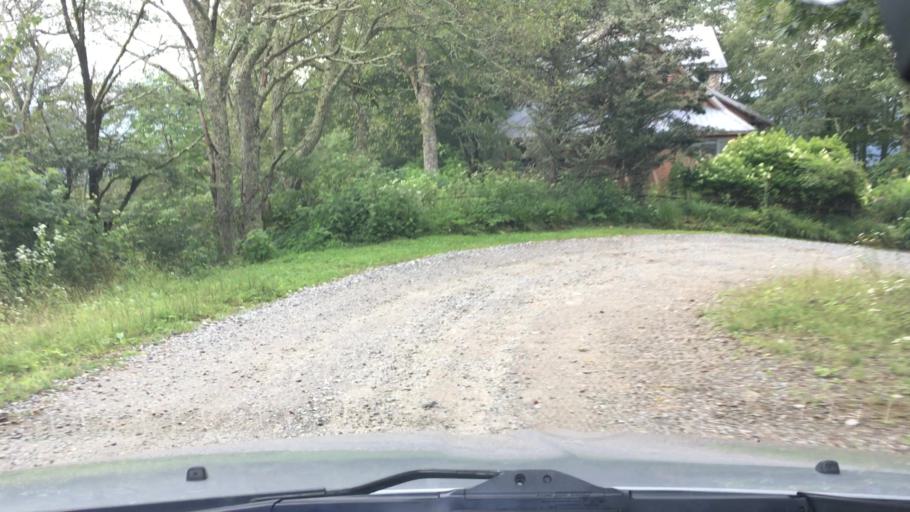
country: US
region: Tennessee
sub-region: Unicoi County
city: Banner Hill
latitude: 35.9866
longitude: -82.4876
